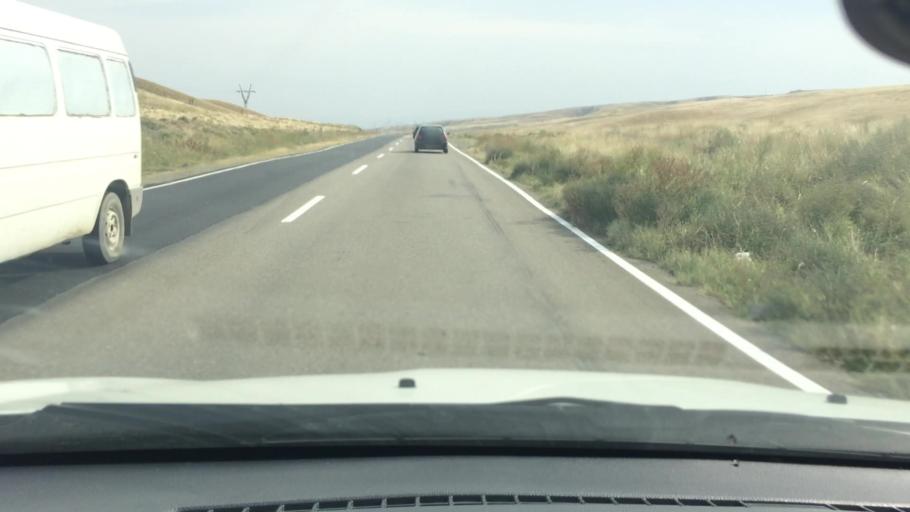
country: GE
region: Kvemo Kartli
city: Rust'avi
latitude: 41.5125
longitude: 44.9470
